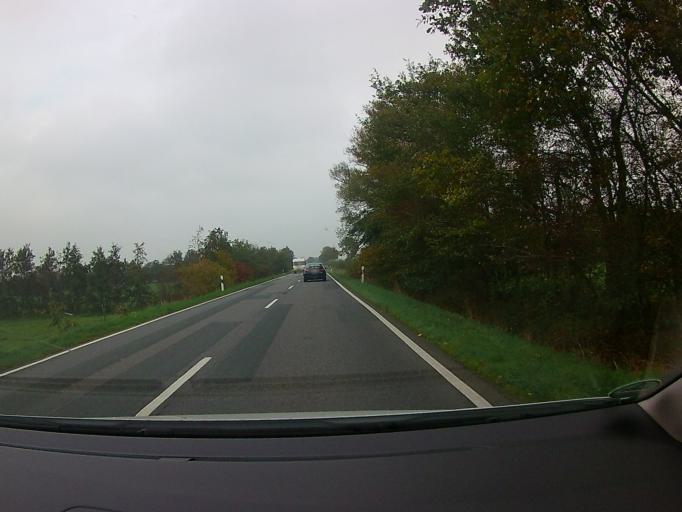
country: DE
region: Schleswig-Holstein
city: Wanderup
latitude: 54.6971
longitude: 9.3048
